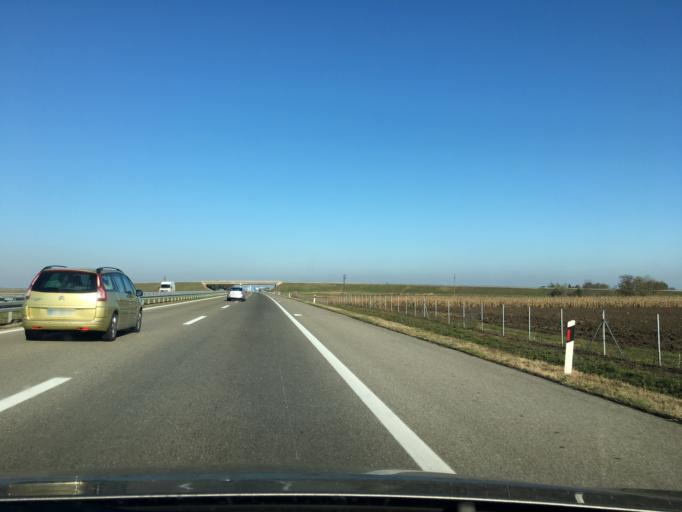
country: RS
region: Autonomna Pokrajina Vojvodina
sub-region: Severnobacki Okrug
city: Backa Topola
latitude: 45.7830
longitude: 19.6981
